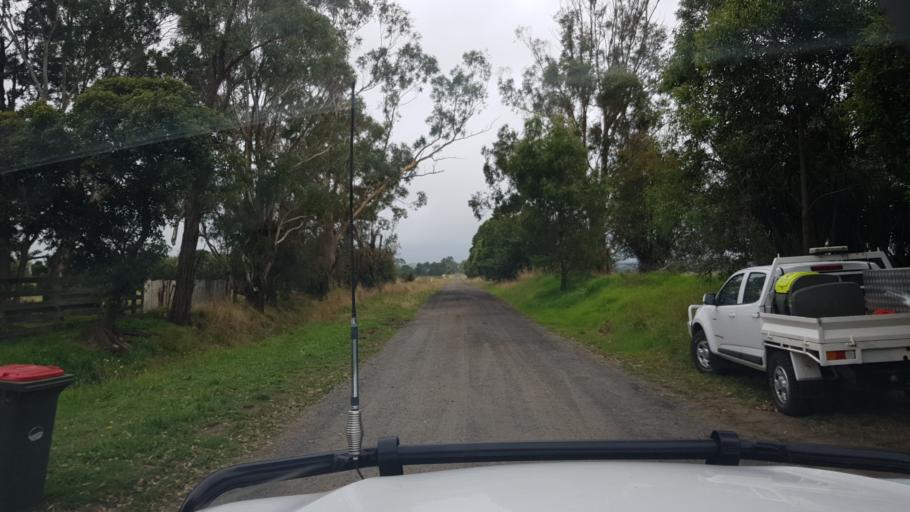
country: AU
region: Victoria
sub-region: Latrobe
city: Moe
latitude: -38.2064
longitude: 146.1082
